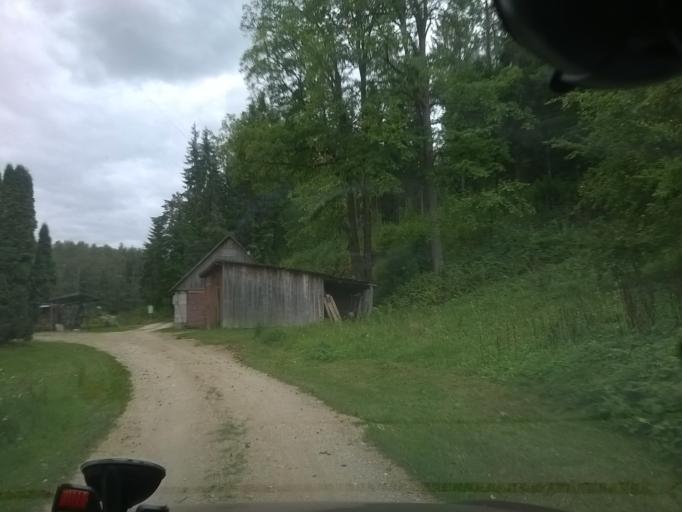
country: EE
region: Vorumaa
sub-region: Voru linn
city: Voru
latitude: 57.8108
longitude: 27.1598
